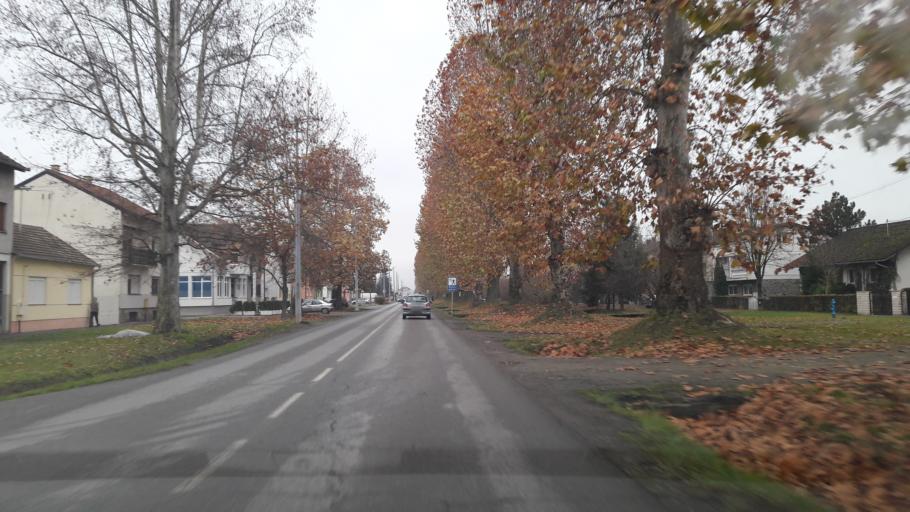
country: HR
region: Osjecko-Baranjska
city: Visnjevac
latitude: 45.5695
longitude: 18.6113
